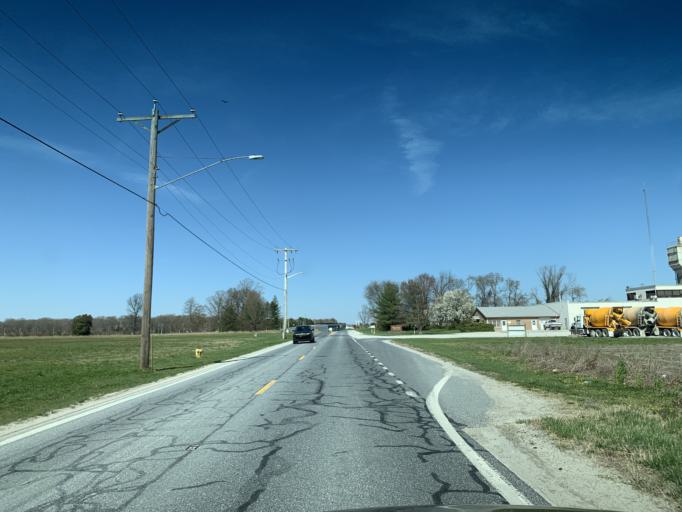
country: US
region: Delaware
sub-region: Sussex County
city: Milford
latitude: 38.9213
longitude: -75.4170
